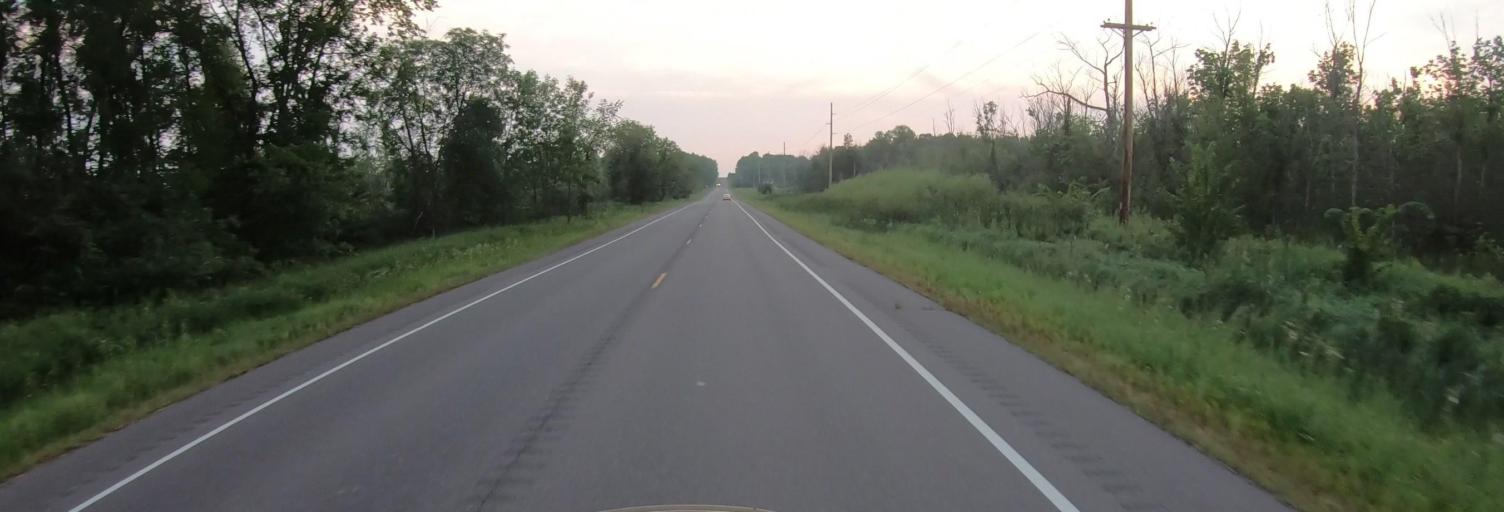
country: US
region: Minnesota
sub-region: Pine County
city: Rock Creek
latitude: 45.7735
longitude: -92.8391
